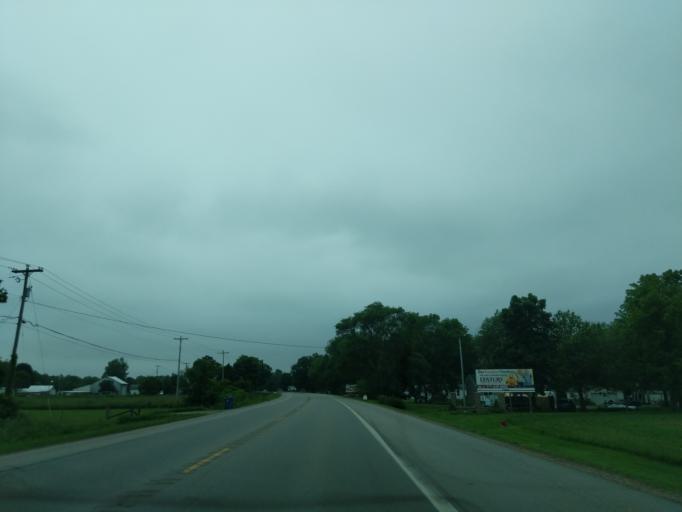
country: US
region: Michigan
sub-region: Branch County
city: Quincy
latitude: 41.9492
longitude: -84.8595
